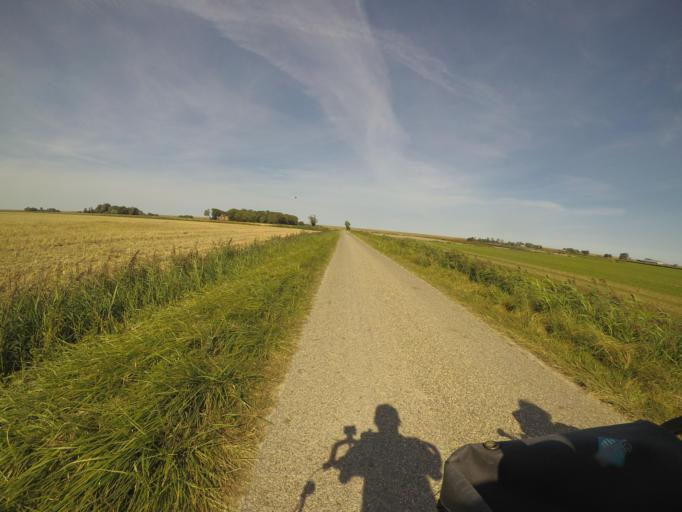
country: NL
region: Friesland
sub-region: Gemeente Ferwerderadiel
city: Ferwert
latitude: 53.3405
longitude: 5.8128
